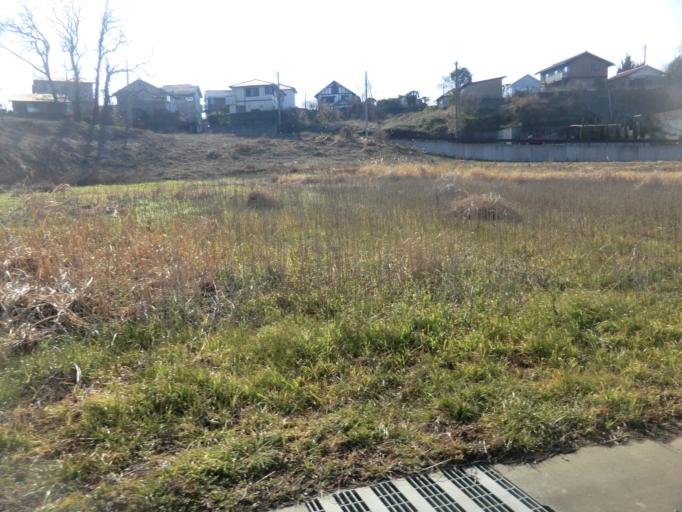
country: JP
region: Ibaraki
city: Naka
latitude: 36.0857
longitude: 140.1389
